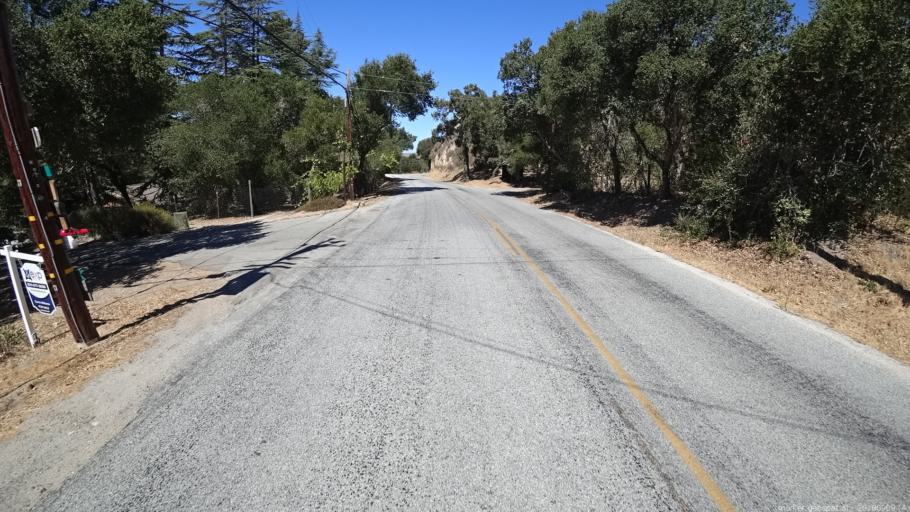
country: US
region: California
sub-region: Monterey County
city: Carmel Valley Village
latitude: 36.5592
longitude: -121.6988
